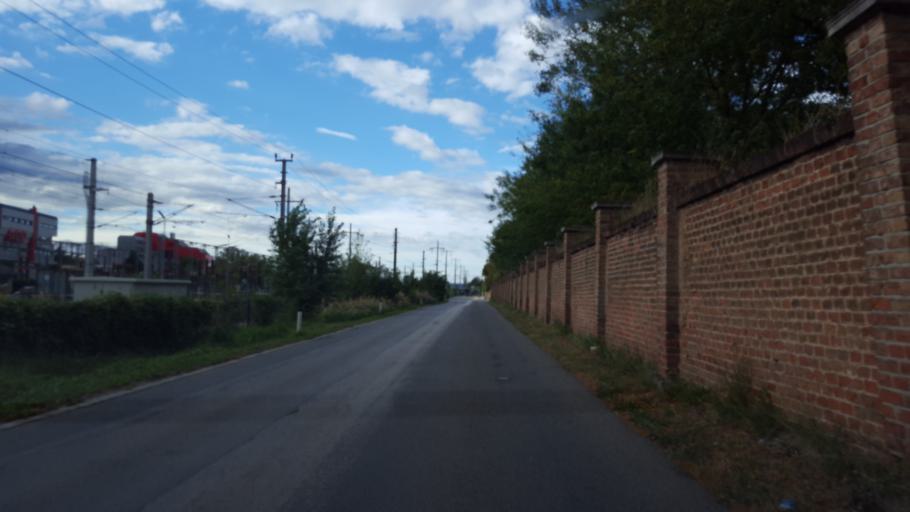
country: AT
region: Lower Austria
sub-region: Politischer Bezirk Wien-Umgebung
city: Schwechat
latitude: 48.1507
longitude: 16.4285
